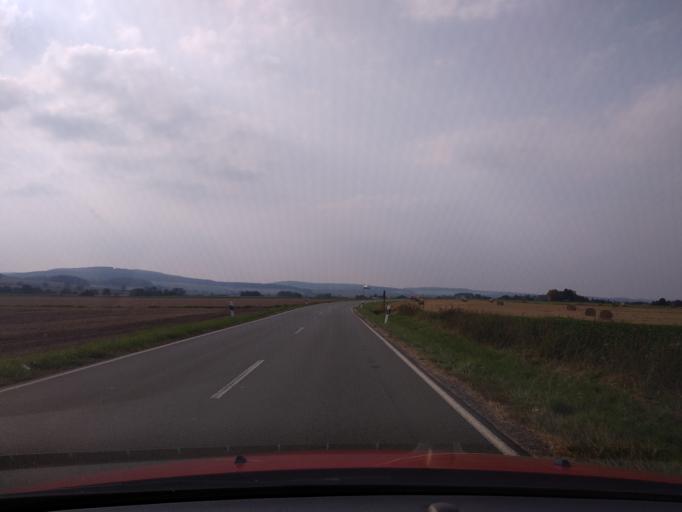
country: DE
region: Hesse
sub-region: Regierungsbezirk Kassel
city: Zierenberg
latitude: 51.4249
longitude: 9.3363
